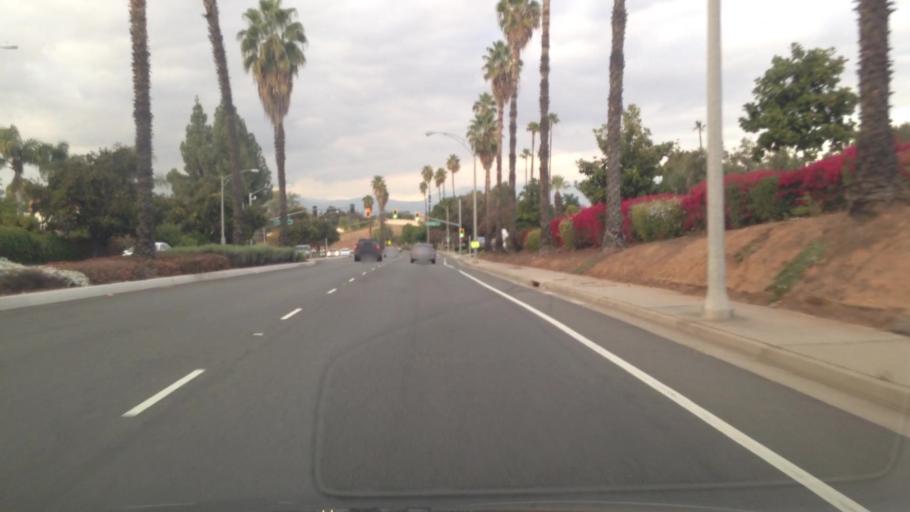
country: US
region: California
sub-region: Riverside County
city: Riverside
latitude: 33.9503
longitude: -117.3589
